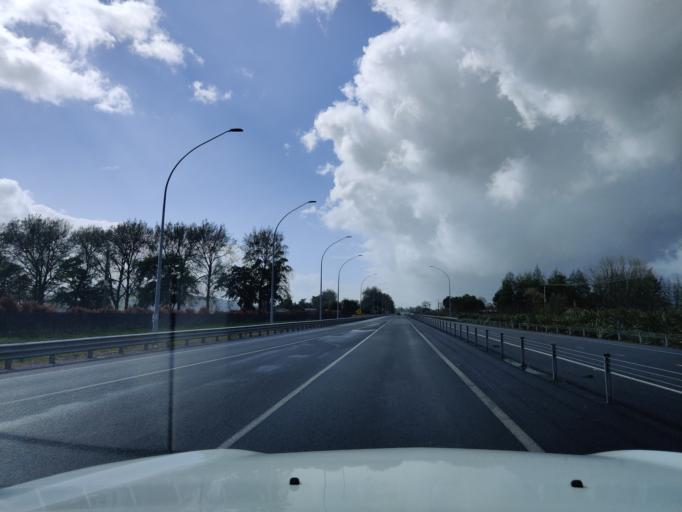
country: NZ
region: Waikato
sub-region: Waipa District
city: Cambridge
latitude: -37.8972
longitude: 175.5087
